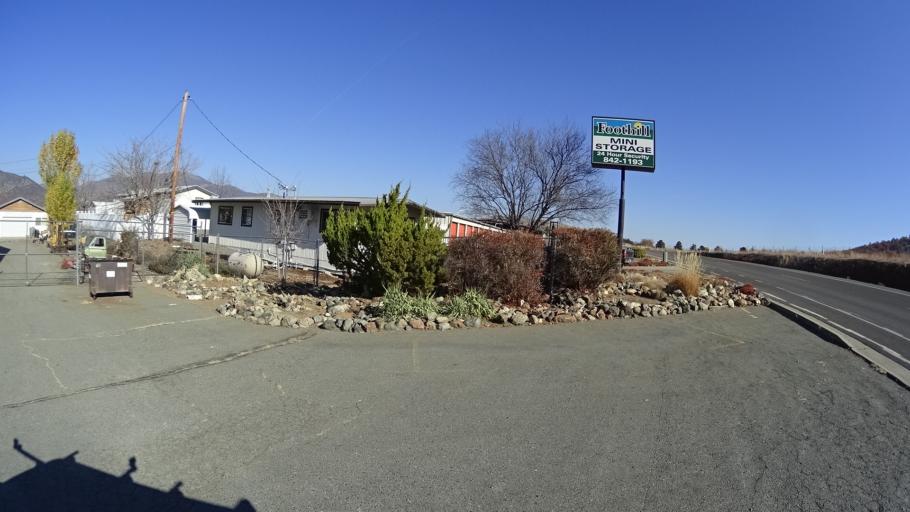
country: US
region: California
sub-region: Siskiyou County
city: Yreka
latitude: 41.7352
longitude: -122.6238
